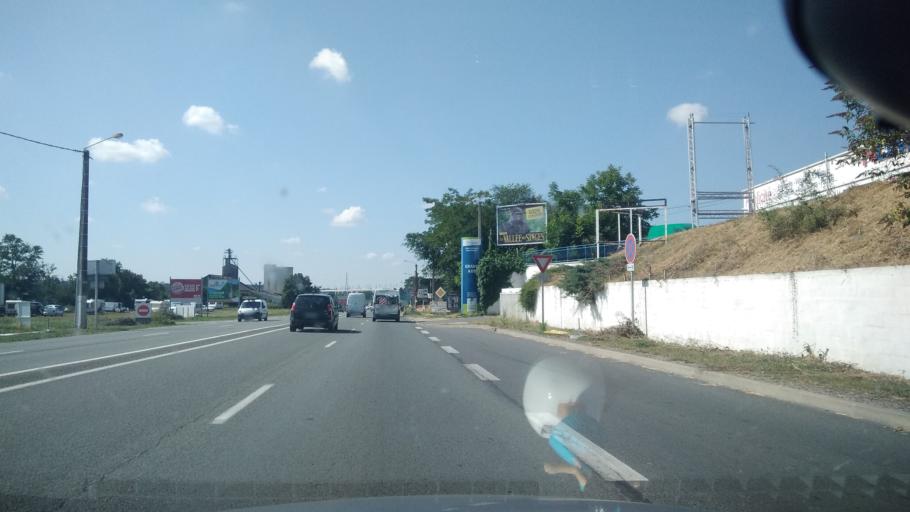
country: FR
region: Poitou-Charentes
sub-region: Departement de la Vienne
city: Chasseneuil-du-Poitou
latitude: 46.6313
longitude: 0.3566
